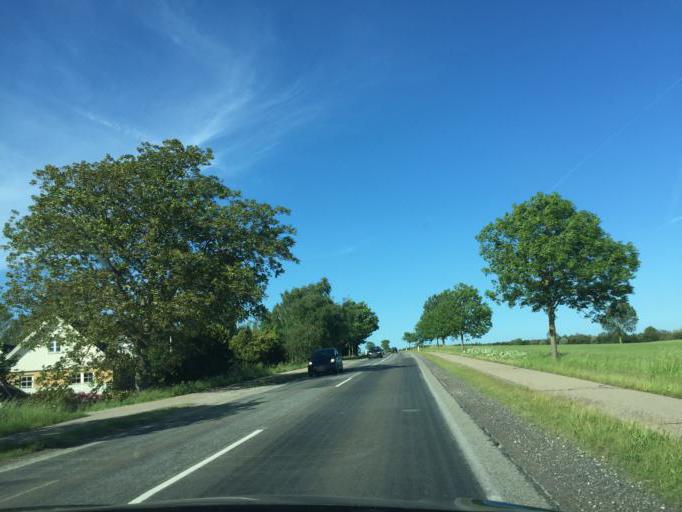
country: DK
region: Zealand
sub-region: Stevns Kommune
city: Harlev
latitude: 55.3632
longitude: 12.2516
